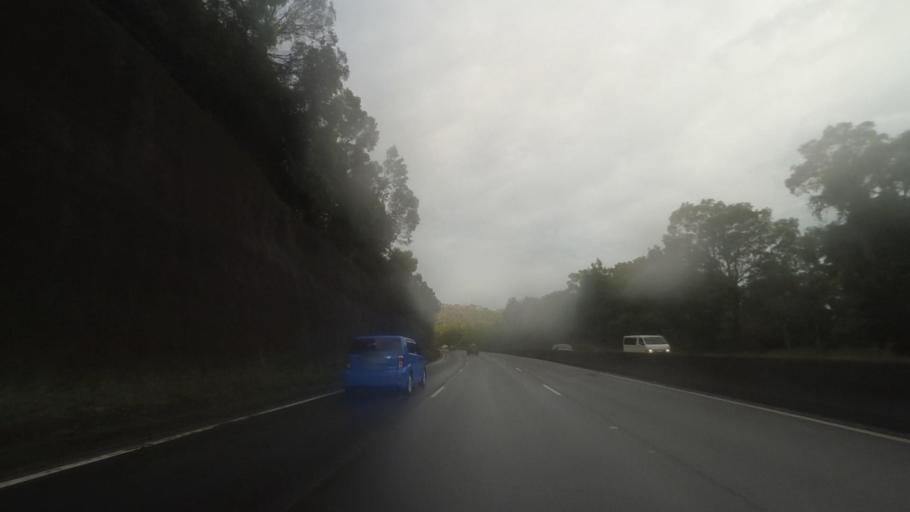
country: AU
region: New South Wales
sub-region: Wollongong
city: Mount Ousley
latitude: -34.3796
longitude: 150.8605
